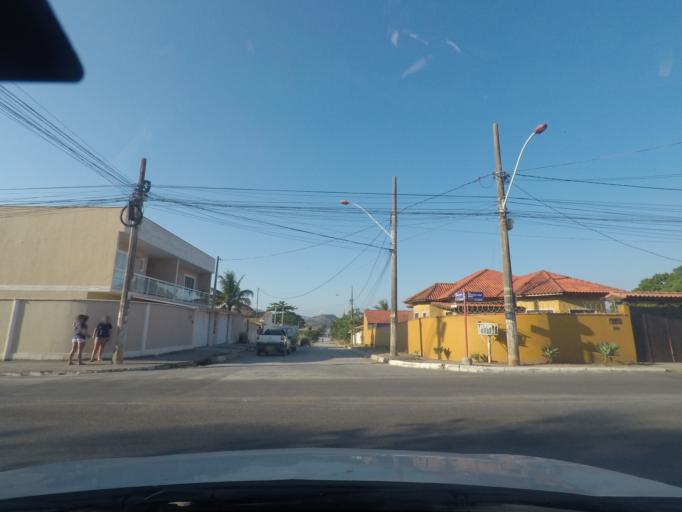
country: BR
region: Rio de Janeiro
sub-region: Marica
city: Marica
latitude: -22.9671
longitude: -42.9351
